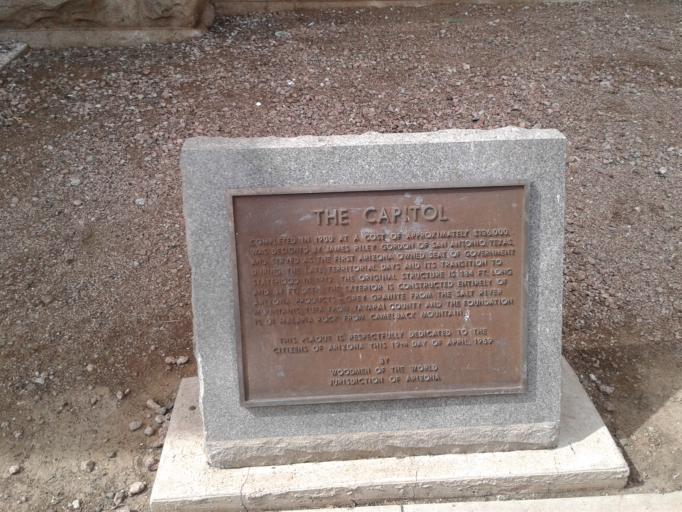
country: US
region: Arizona
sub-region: Maricopa County
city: Phoenix
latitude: 33.4482
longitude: -112.0968
